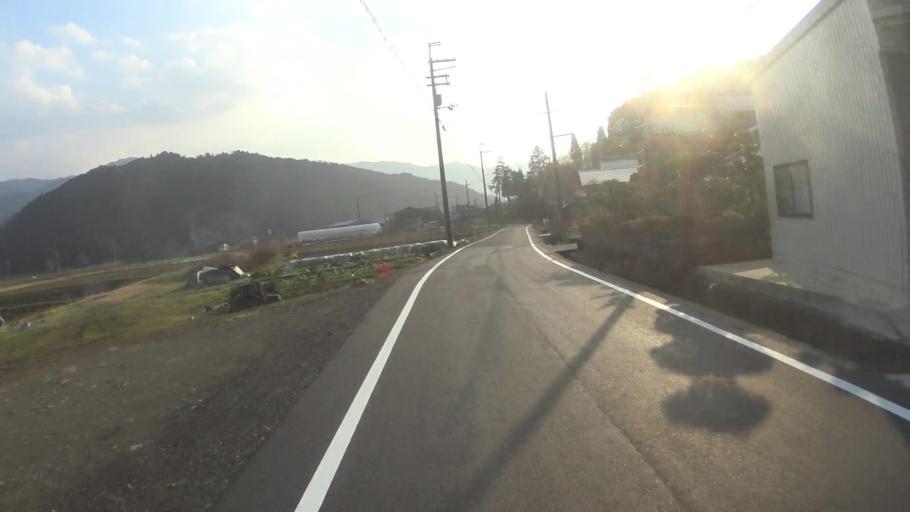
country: JP
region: Kyoto
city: Maizuru
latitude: 35.3717
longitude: 135.4181
